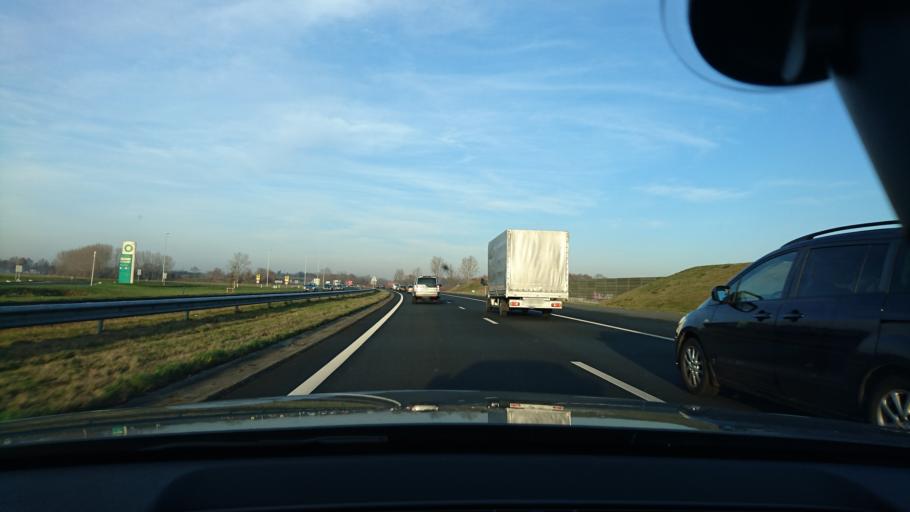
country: NL
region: North Brabant
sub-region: Gemeente Son en Breugel
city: Son
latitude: 51.5354
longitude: 5.4802
